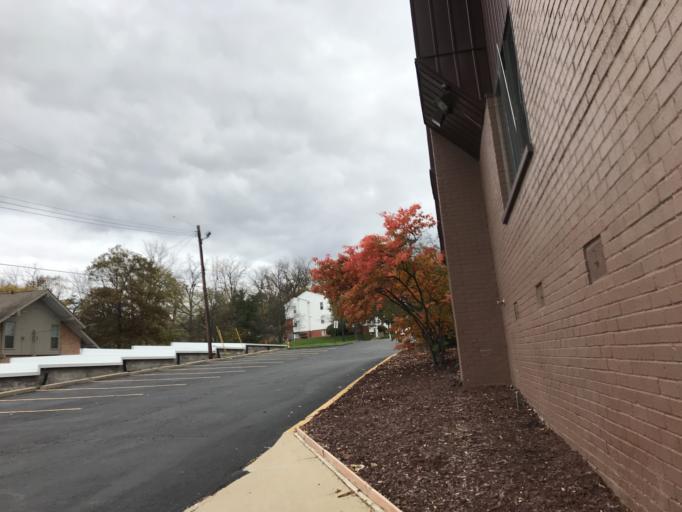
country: US
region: Michigan
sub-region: Washtenaw County
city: Ann Arbor
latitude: 42.2510
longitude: -83.7235
